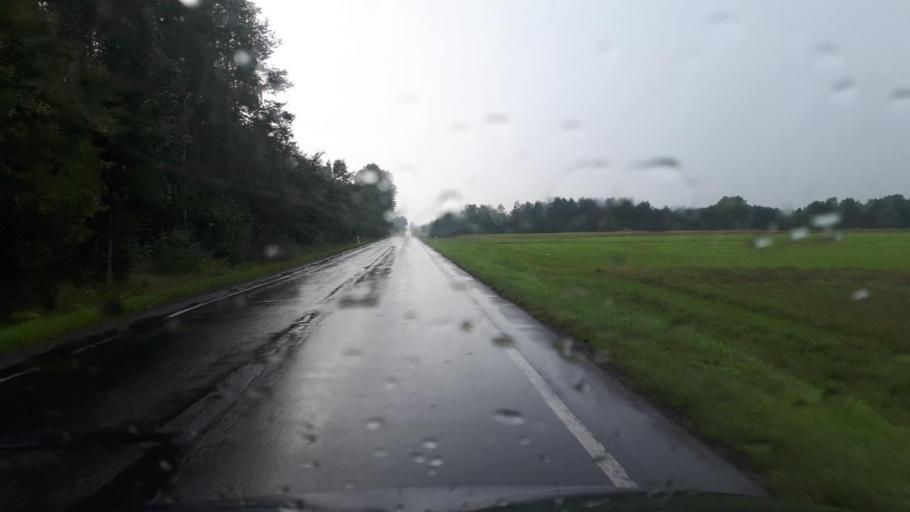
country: PL
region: Silesian Voivodeship
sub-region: Powiat gliwicki
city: Wielowies
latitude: 50.5287
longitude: 18.6537
